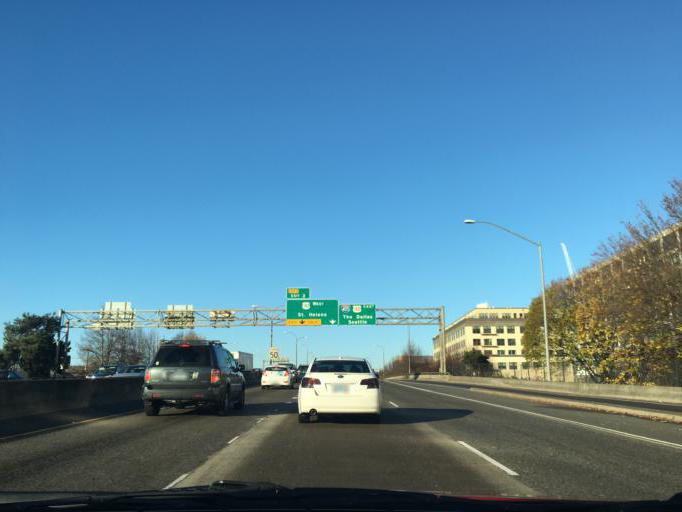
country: US
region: Oregon
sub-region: Multnomah County
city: Portland
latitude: 45.5281
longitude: -122.6868
